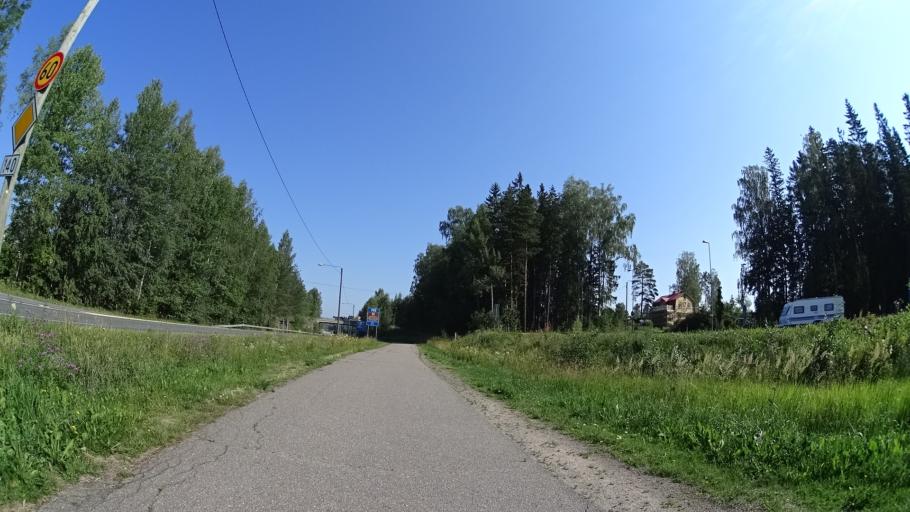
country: FI
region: Uusimaa
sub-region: Helsinki
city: Kerava
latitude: 60.3435
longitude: 25.1268
